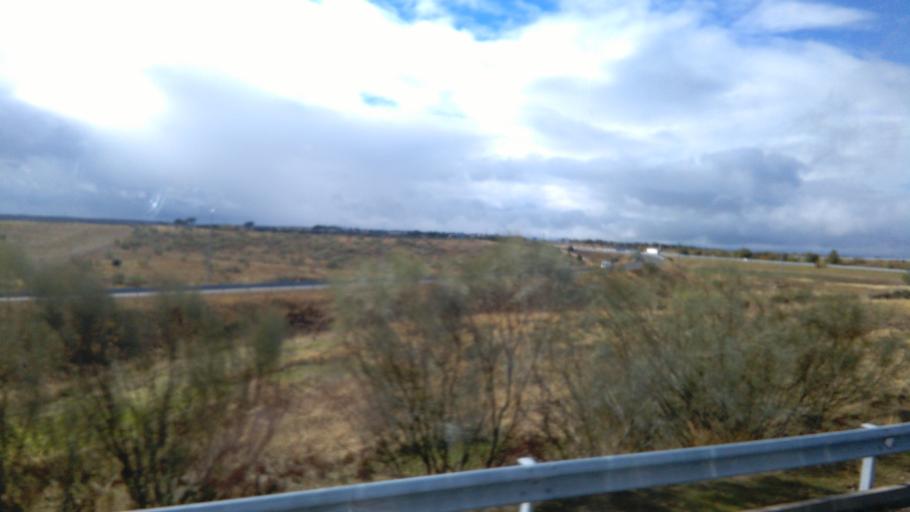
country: ES
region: Madrid
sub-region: Provincia de Madrid
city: Navalcarnero
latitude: 40.2672
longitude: -4.0335
